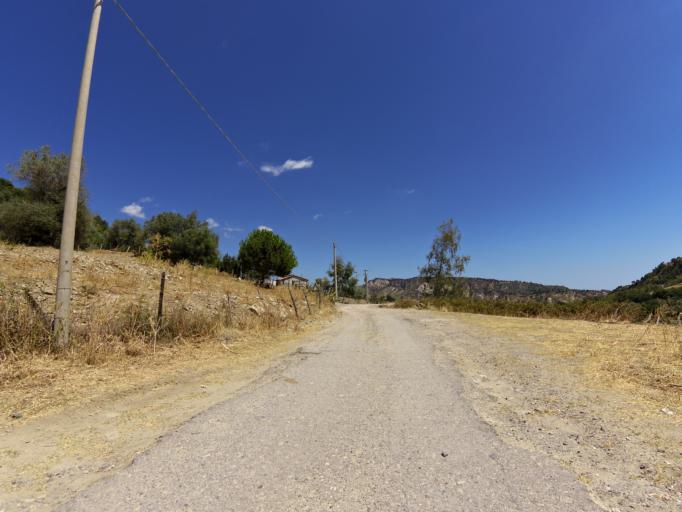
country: IT
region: Calabria
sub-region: Provincia di Reggio Calabria
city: Stilo
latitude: 38.4633
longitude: 16.4678
